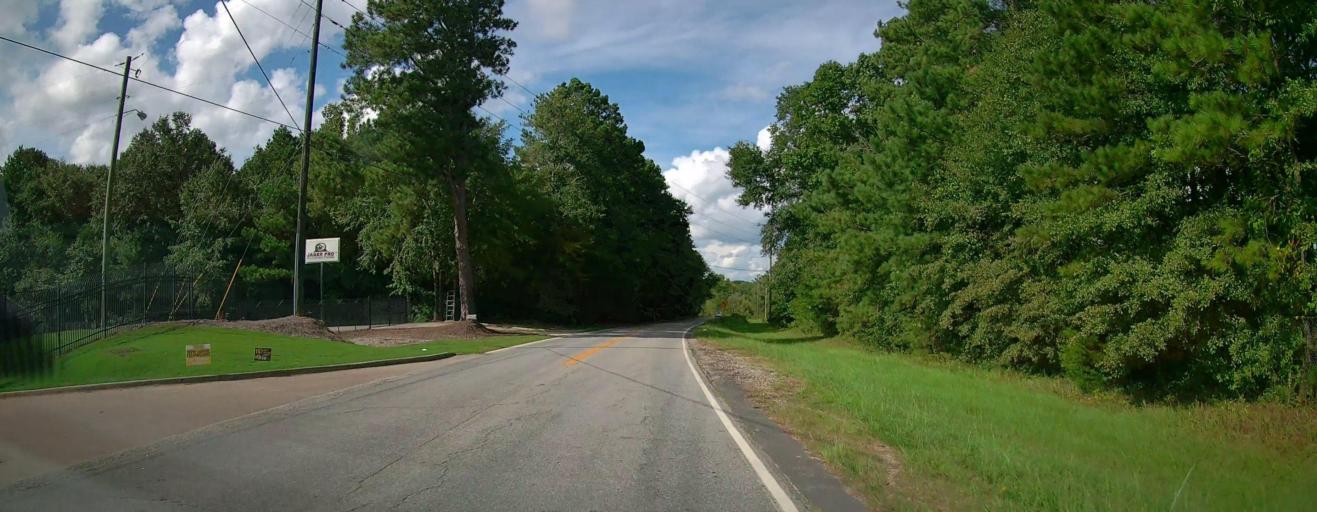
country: US
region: Alabama
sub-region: Russell County
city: Phenix City
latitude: 32.5984
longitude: -84.9490
